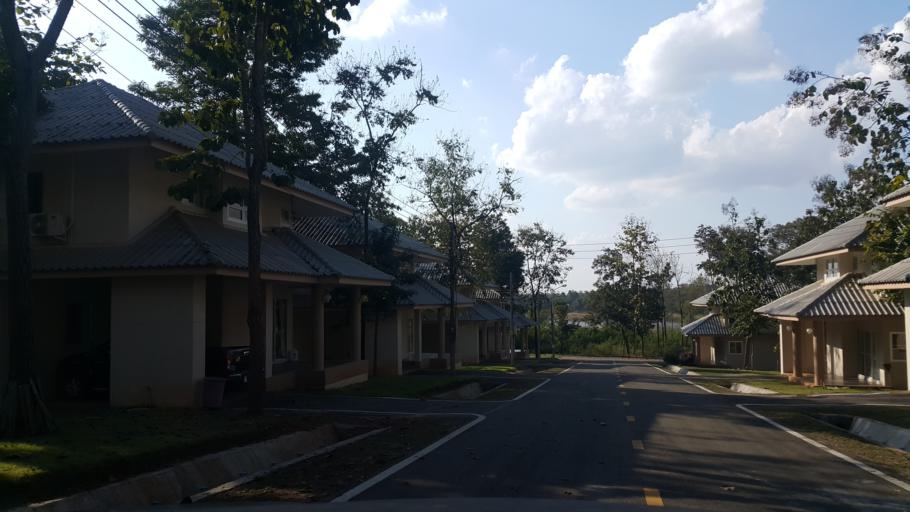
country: TH
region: Lamphun
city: Mae Tha
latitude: 18.5155
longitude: 99.1185
